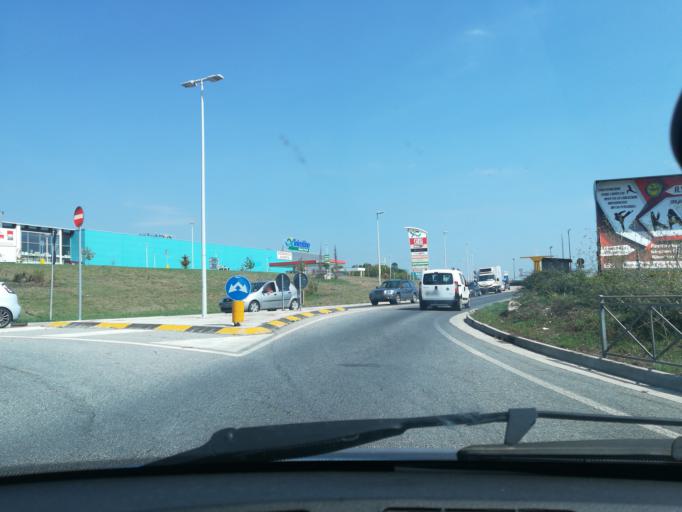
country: IT
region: The Marches
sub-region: Provincia di Macerata
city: Tolentino
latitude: 43.2156
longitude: 13.3091
